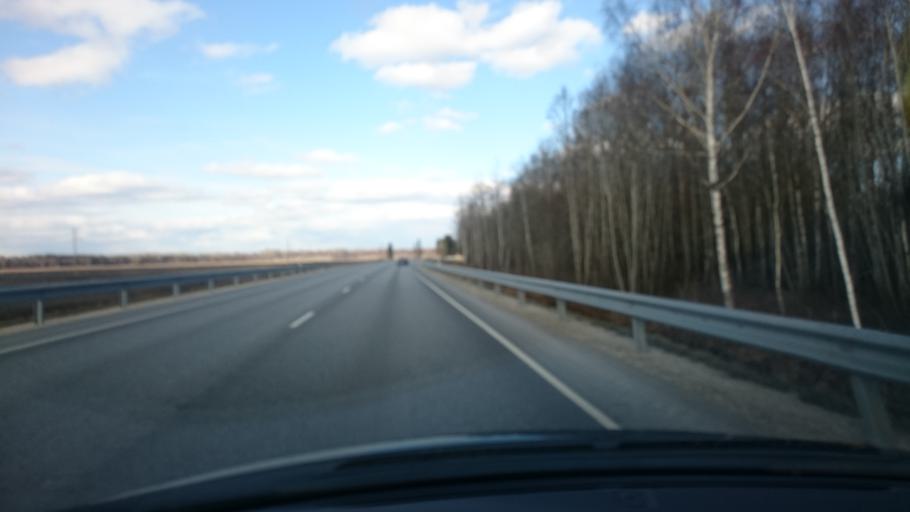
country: EE
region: Laeaene
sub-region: Lihula vald
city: Lihula
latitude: 58.7786
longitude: 23.9945
